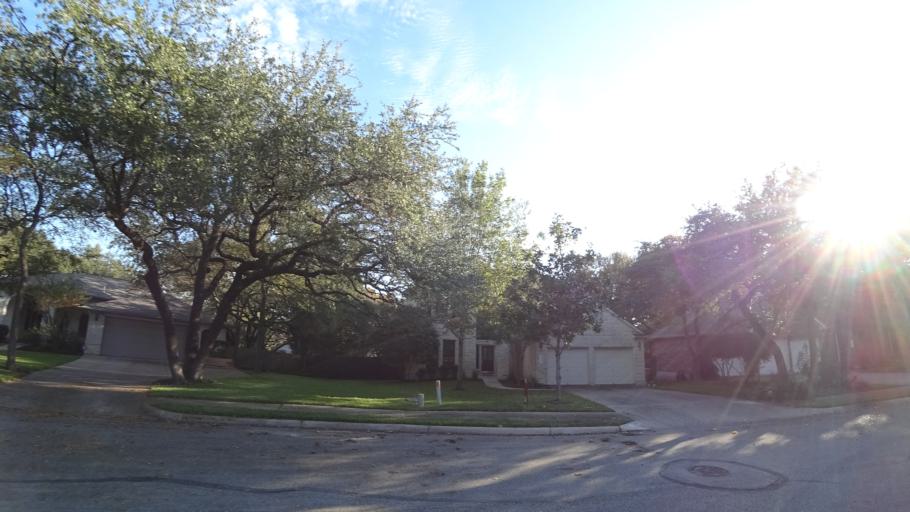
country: US
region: Texas
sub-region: Williamson County
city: Anderson Mill
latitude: 30.4429
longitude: -97.8020
